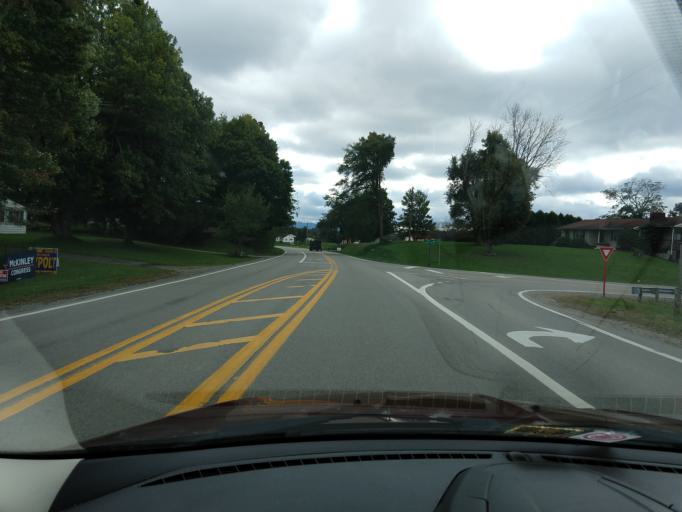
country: US
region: West Virginia
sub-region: Barbour County
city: Belington
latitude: 39.0621
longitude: -79.9718
